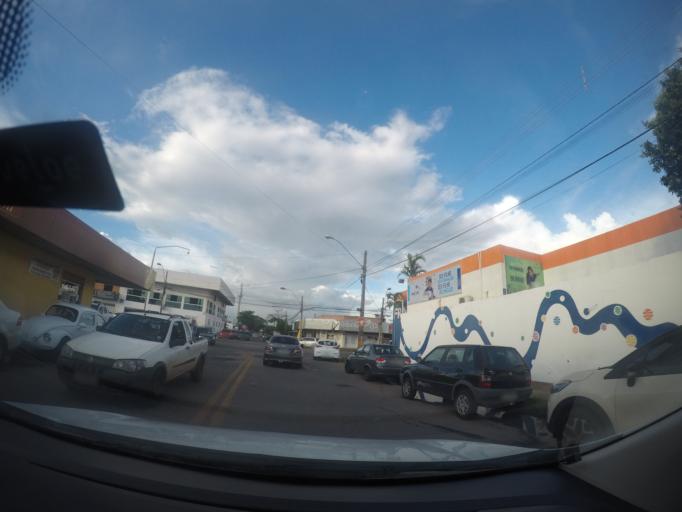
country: BR
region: Goias
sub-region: Goiania
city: Goiania
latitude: -16.6810
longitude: -49.3164
